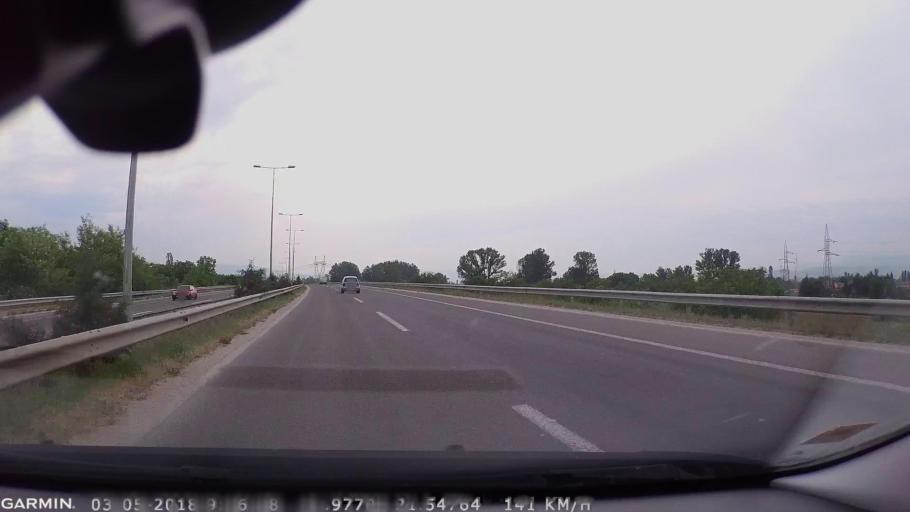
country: MK
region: Ilinden
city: Jurumleri
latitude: 41.9762
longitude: 21.5496
